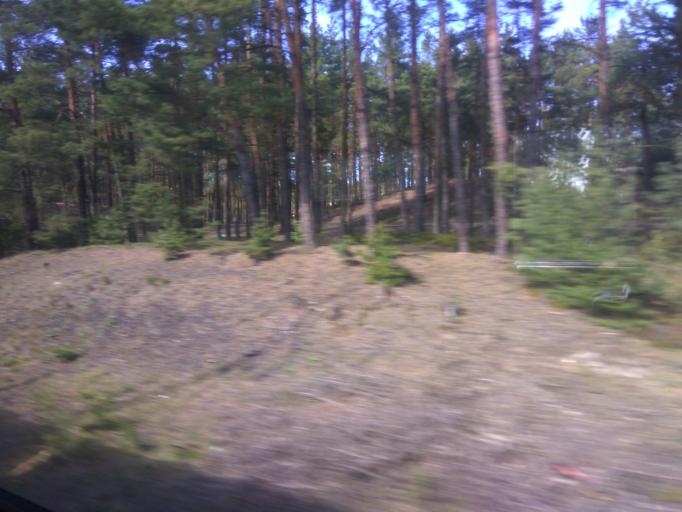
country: LV
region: Babite
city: Pinki
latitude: 56.9700
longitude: 23.8927
